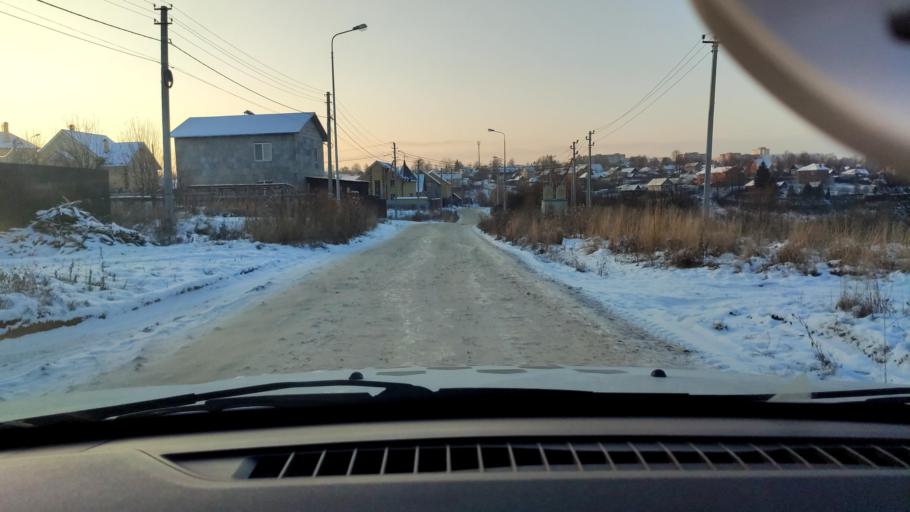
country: RU
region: Perm
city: Perm
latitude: 58.0284
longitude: 56.3479
